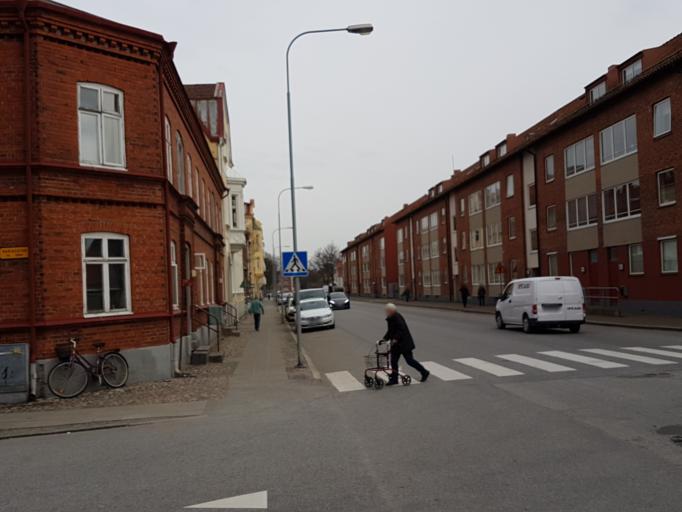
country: SE
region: Skane
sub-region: Ystads Kommun
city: Ystad
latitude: 55.4313
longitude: 13.8326
